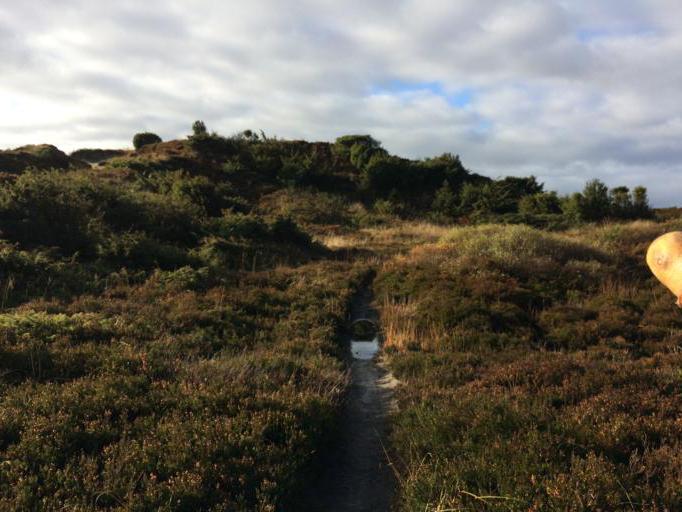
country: DK
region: Central Jutland
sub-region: Holstebro Kommune
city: Ulfborg
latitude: 56.2542
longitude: 8.4132
